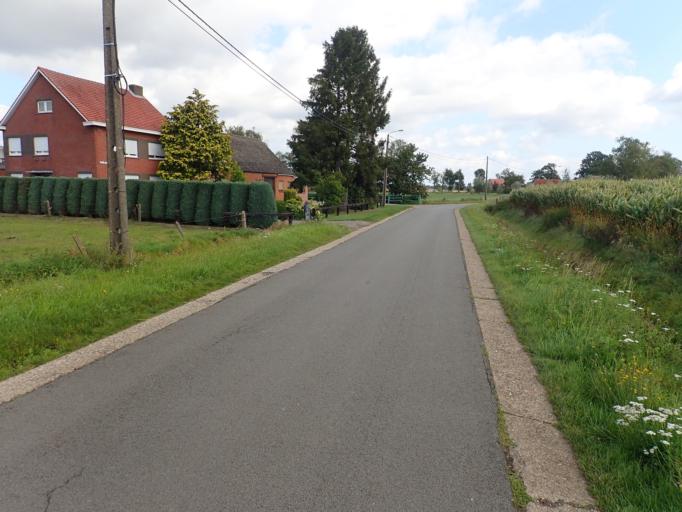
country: BE
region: Flanders
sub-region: Provincie Antwerpen
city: Herenthout
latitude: 51.1380
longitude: 4.7861
